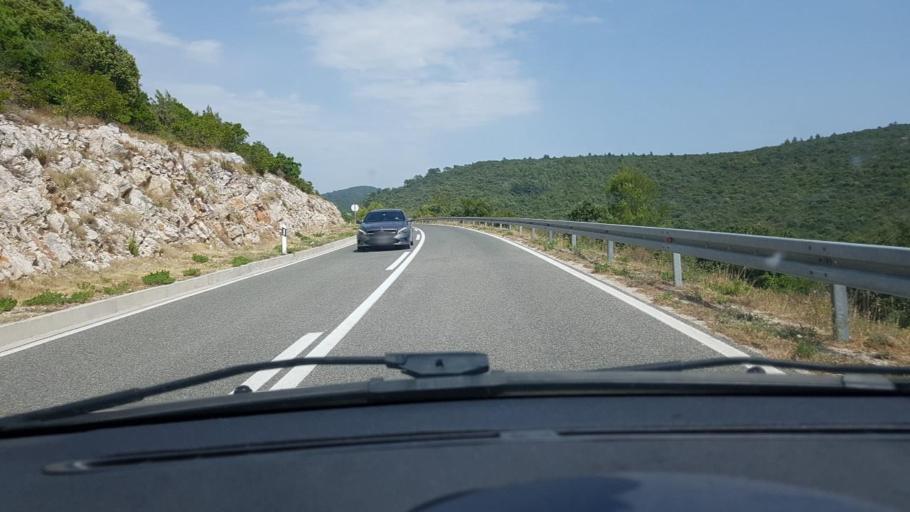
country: HR
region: Dubrovacko-Neretvanska
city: Smokvica
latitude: 42.9553
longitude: 16.9277
